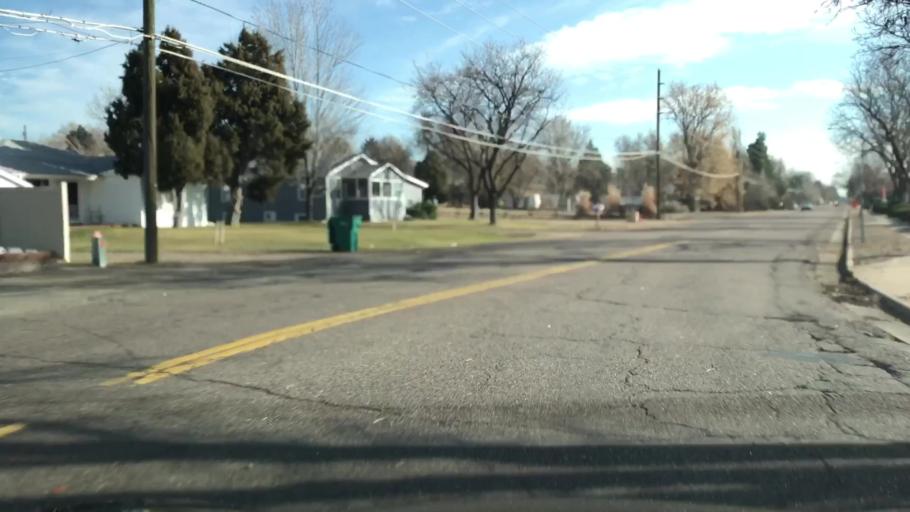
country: US
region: Colorado
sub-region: Arapahoe County
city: Glendale
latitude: 39.6955
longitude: -104.9025
